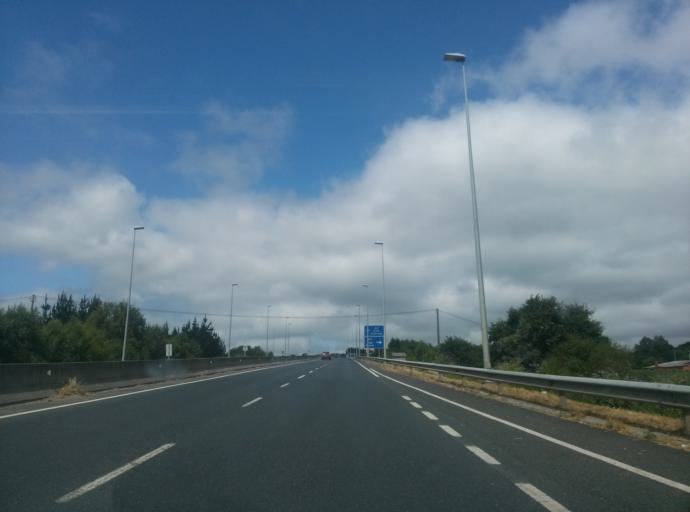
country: ES
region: Galicia
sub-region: Provincia de Lugo
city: Lugo
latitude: 43.0551
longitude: -7.5626
